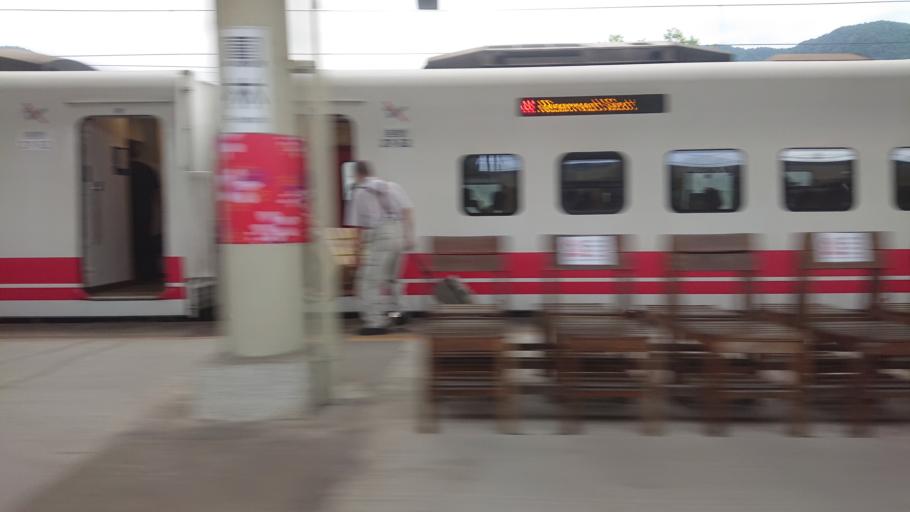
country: TW
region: Taiwan
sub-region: Hualien
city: Hualian
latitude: 23.7468
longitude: 121.4470
